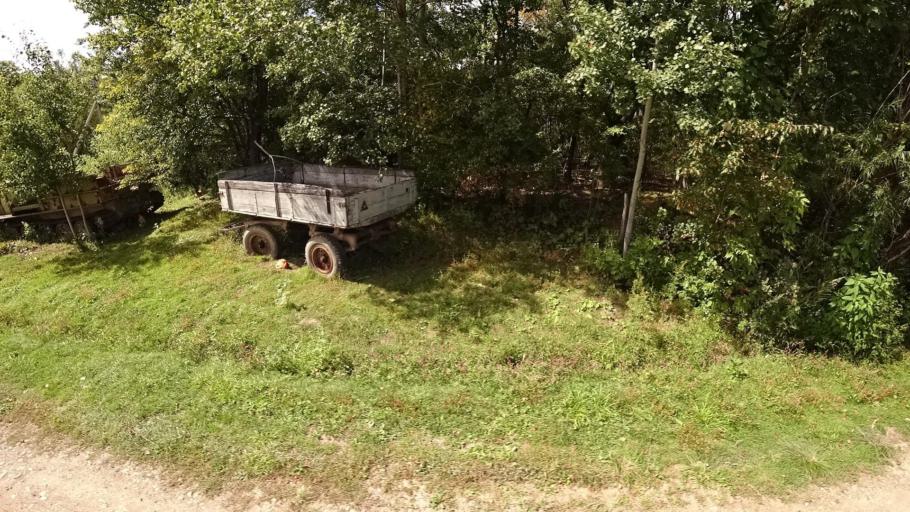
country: RU
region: Primorskiy
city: Yakovlevka
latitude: 44.6483
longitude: 133.5948
